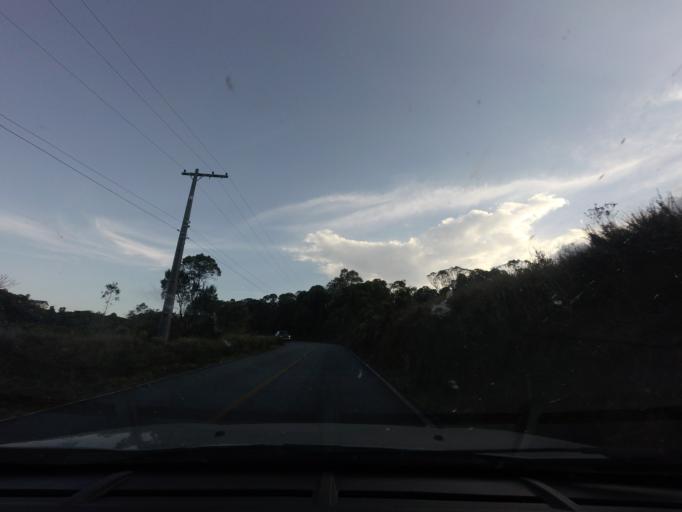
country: BR
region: Sao Paulo
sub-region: Campos Do Jordao
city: Campos do Jordao
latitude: -22.7648
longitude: -45.5452
